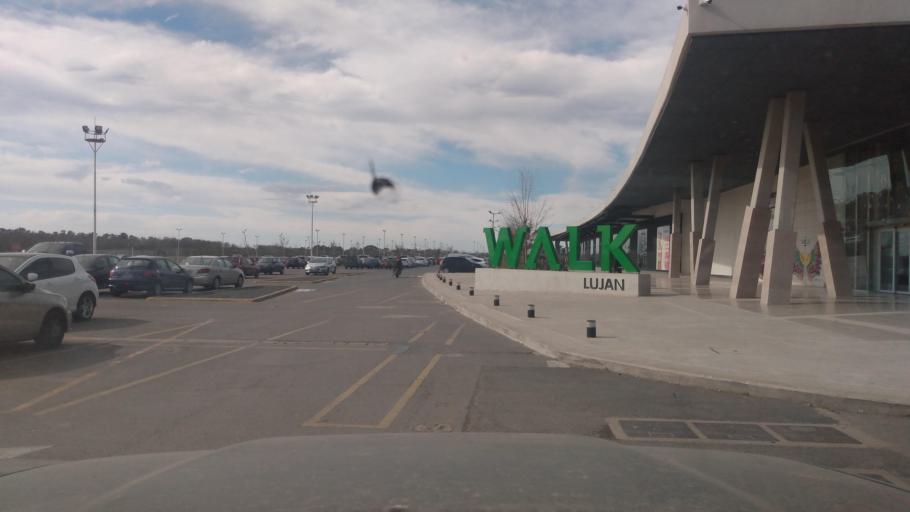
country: AR
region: Buenos Aires
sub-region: Partido de Lujan
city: Lujan
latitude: -34.5468
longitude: -59.1113
